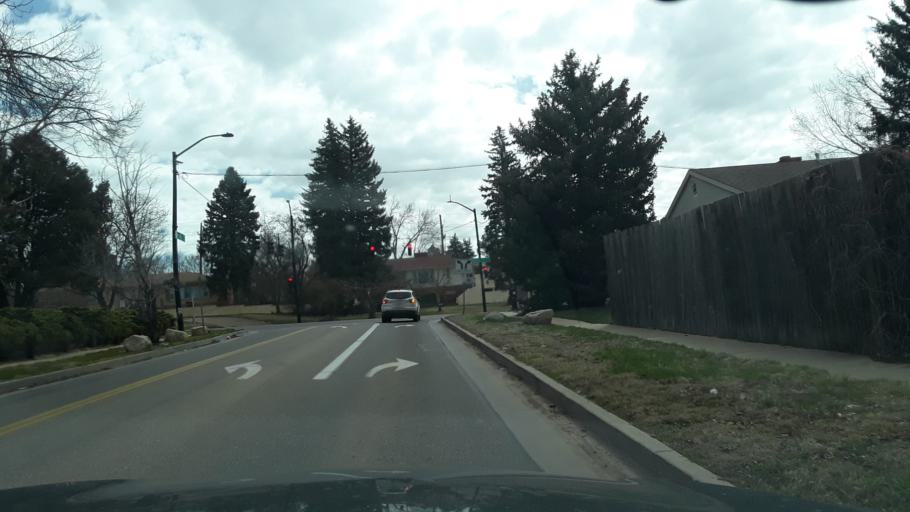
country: US
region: Colorado
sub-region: El Paso County
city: Colorado Springs
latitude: 38.8497
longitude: -104.7949
